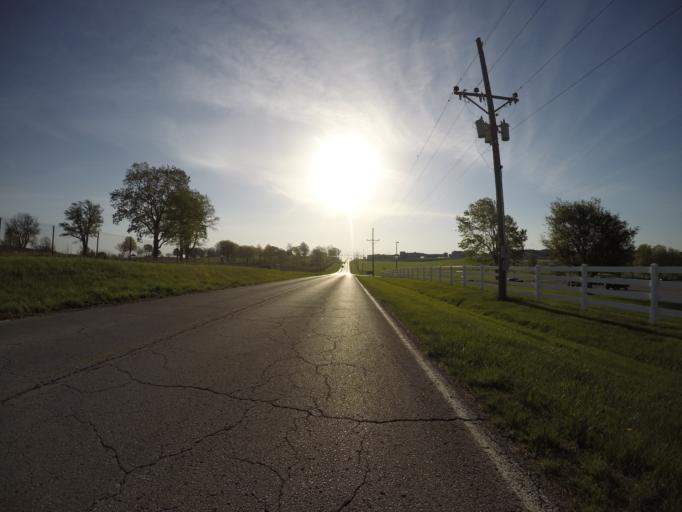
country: US
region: Missouri
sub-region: Jackson County
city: Lees Summit
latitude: 38.9133
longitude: -94.4562
